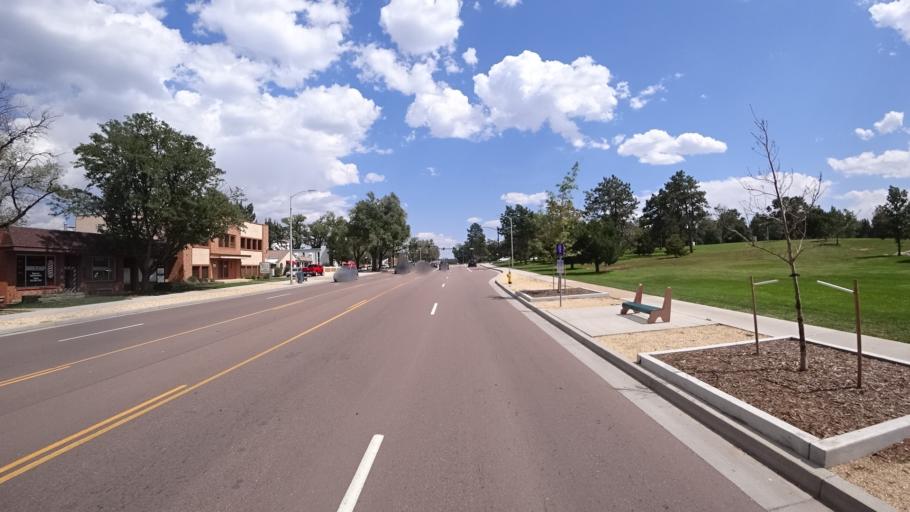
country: US
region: Colorado
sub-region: El Paso County
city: Colorado Springs
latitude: 38.8330
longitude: -104.7960
